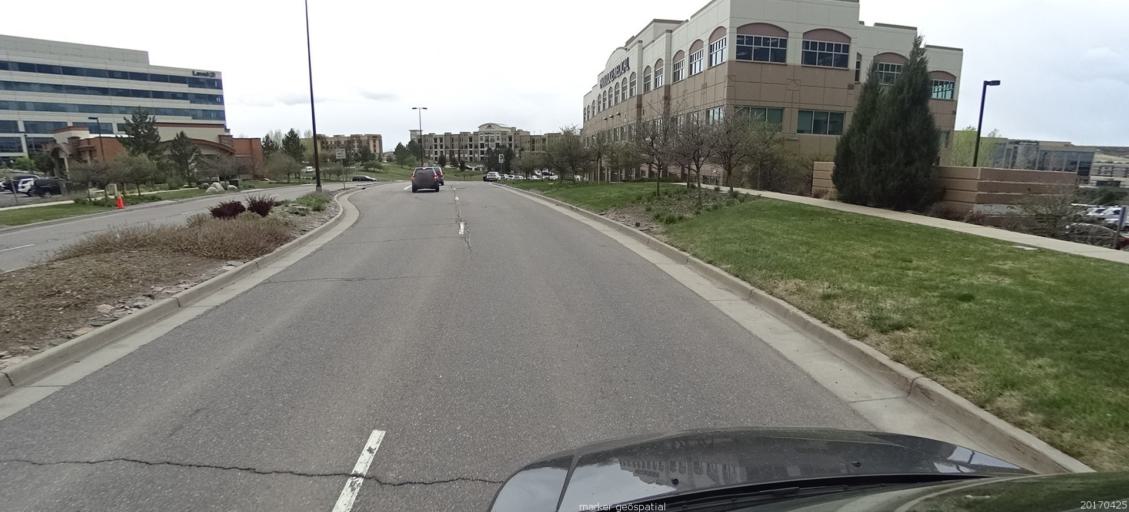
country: US
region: Colorado
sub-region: Adams County
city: Lone Tree
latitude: 39.5384
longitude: -104.8739
